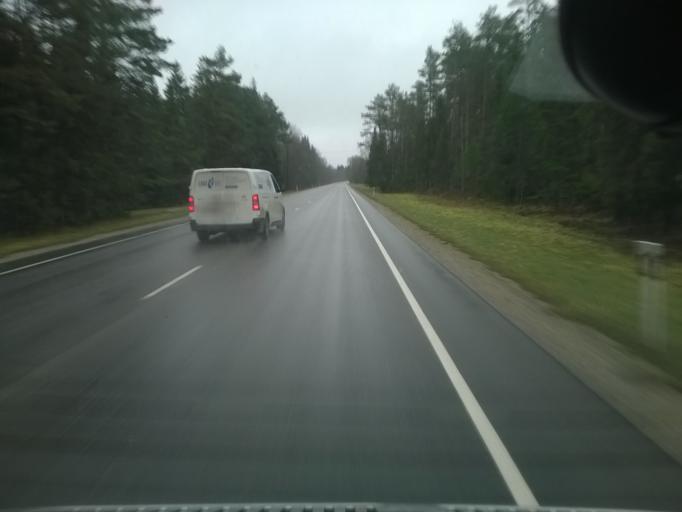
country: EE
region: Harju
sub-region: Nissi vald
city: Turba
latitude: 58.9879
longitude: 24.0156
